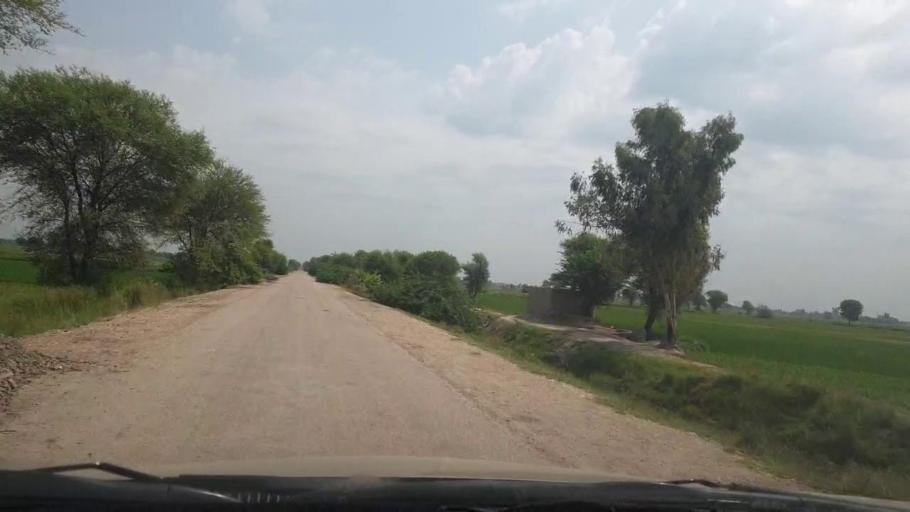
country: PK
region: Sindh
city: Miro Khan
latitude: 27.6869
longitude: 68.1916
